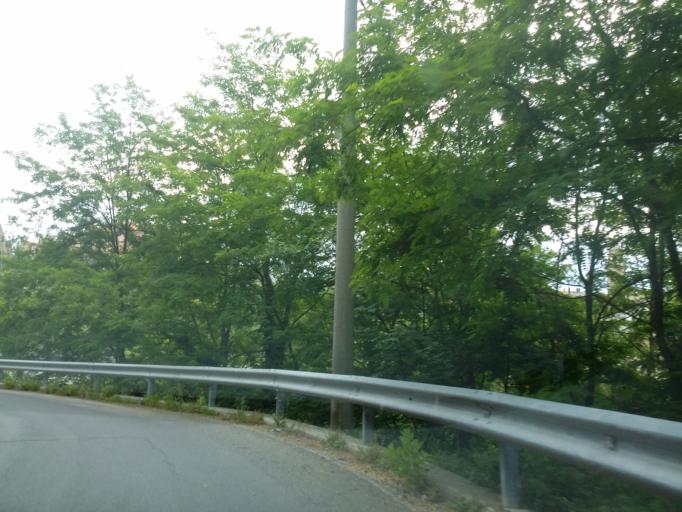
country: IT
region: Liguria
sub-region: Provincia di Savona
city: Orco Feglino
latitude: 44.2230
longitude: 8.3429
